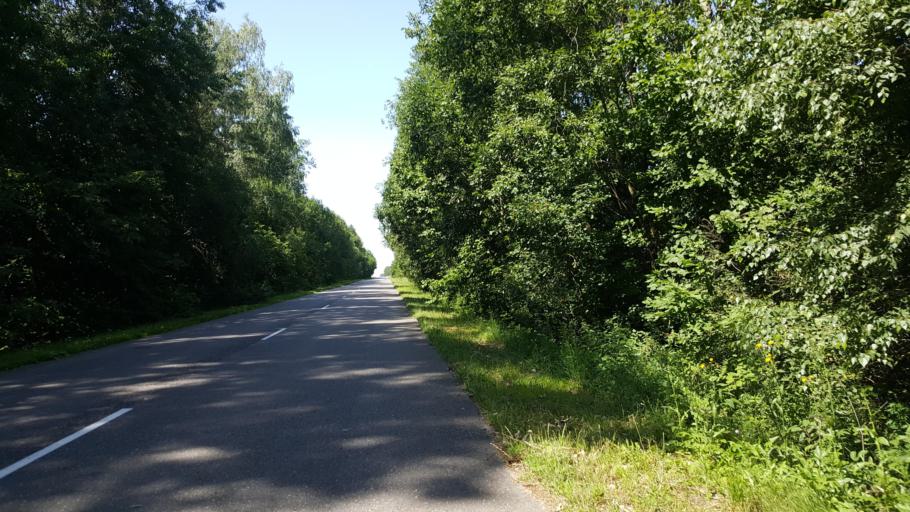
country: BY
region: Brest
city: Kamyanyets
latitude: 52.3769
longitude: 23.6214
